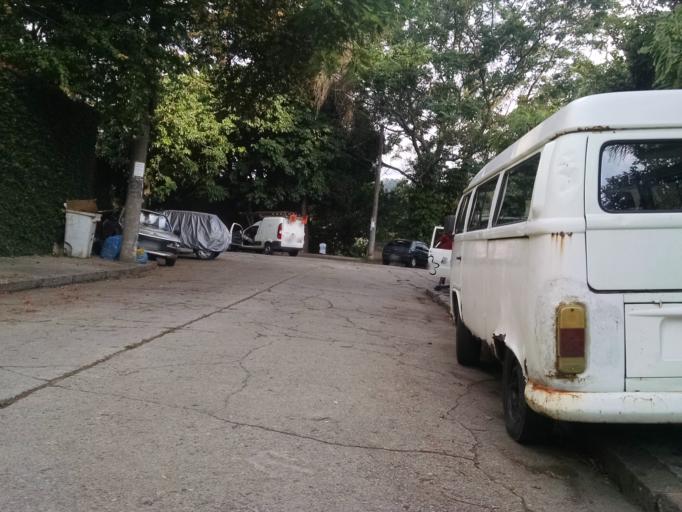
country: BR
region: Rio de Janeiro
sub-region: Rio De Janeiro
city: Rio de Janeiro
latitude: -22.9365
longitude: -43.1991
